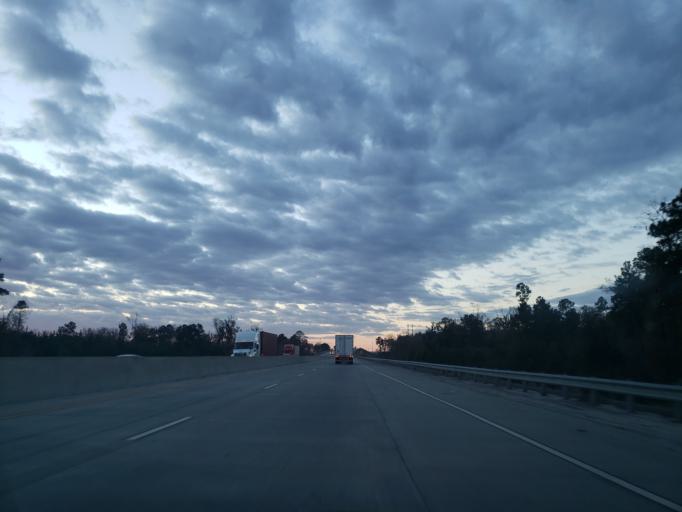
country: US
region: Georgia
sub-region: Chatham County
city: Port Wentworth
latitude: 32.1595
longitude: -81.1774
